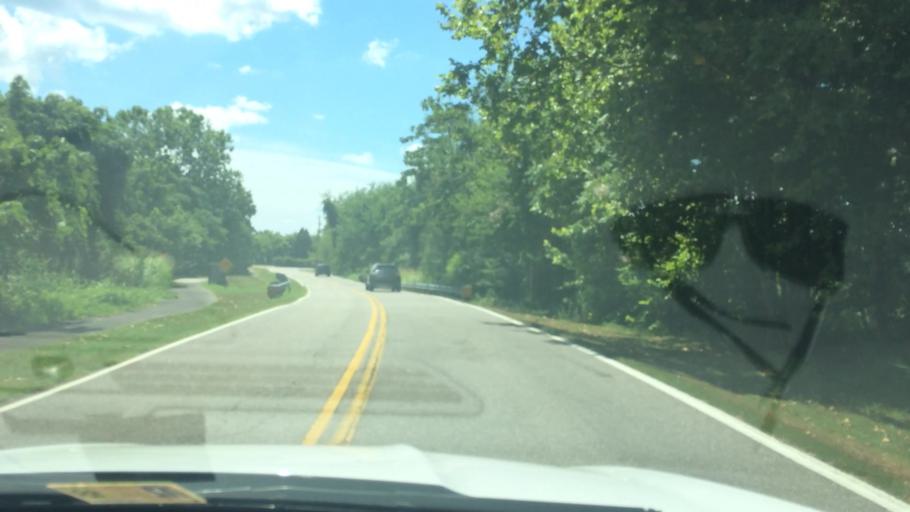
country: US
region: Virginia
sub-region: King William County
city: West Point
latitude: 37.5410
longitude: -76.7946
